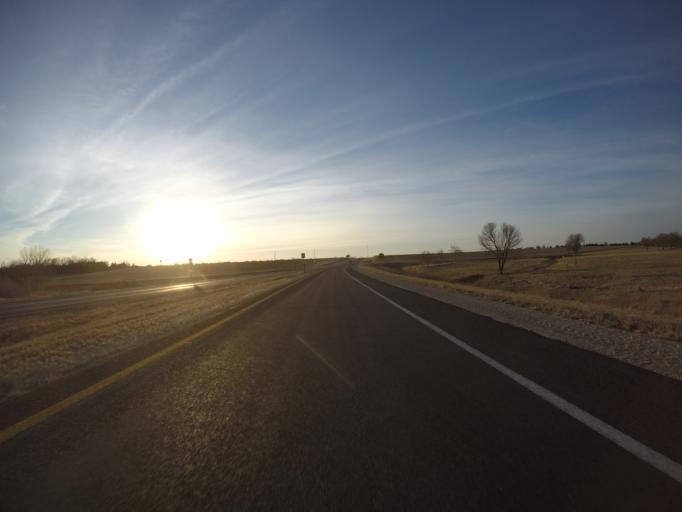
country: US
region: Kansas
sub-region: Riley County
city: Fort Riley North
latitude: 39.2995
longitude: -96.8107
